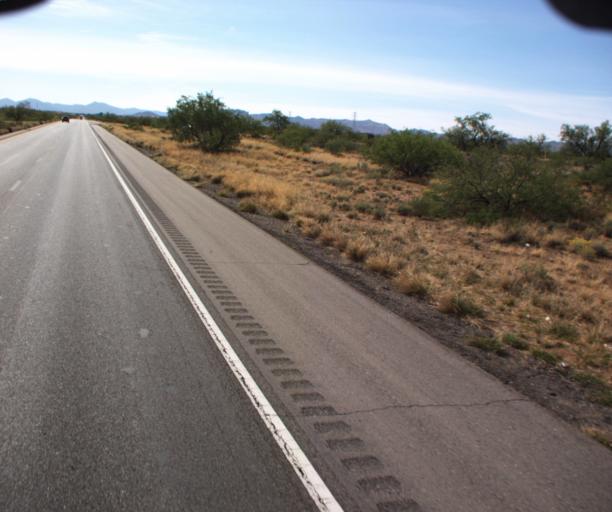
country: US
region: Arizona
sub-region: Pima County
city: Vail
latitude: 32.0265
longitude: -110.7199
